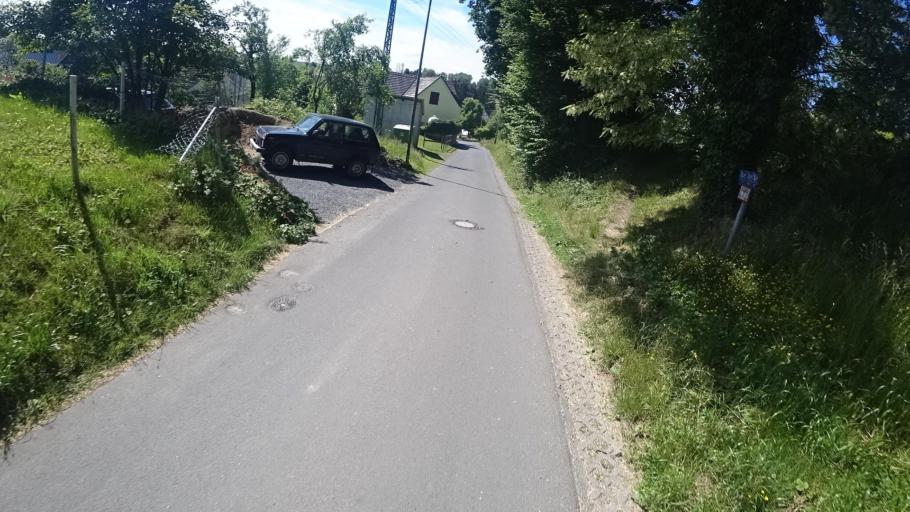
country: DE
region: Rheinland-Pfalz
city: Sorth
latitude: 50.6999
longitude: 7.6850
